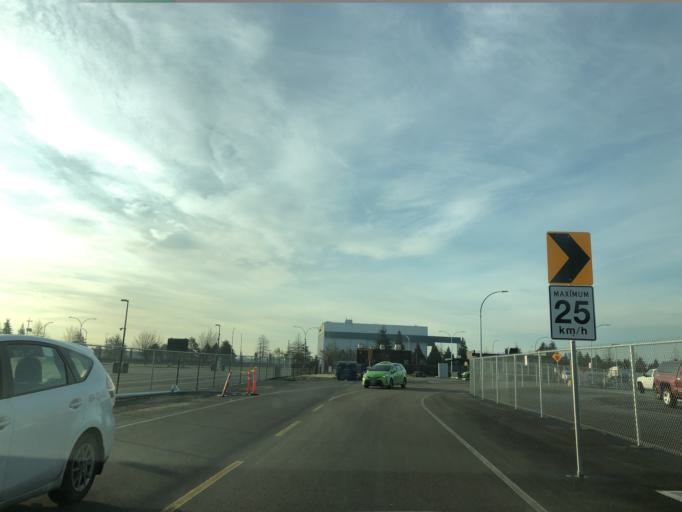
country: CA
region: British Columbia
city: Richmond
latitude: 49.1948
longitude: -123.1620
